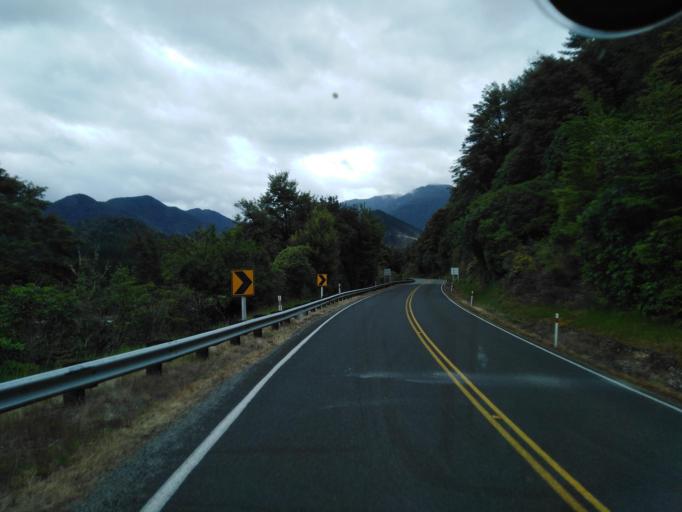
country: NZ
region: Tasman
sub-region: Tasman District
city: Wakefield
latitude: -41.7054
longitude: 172.5866
